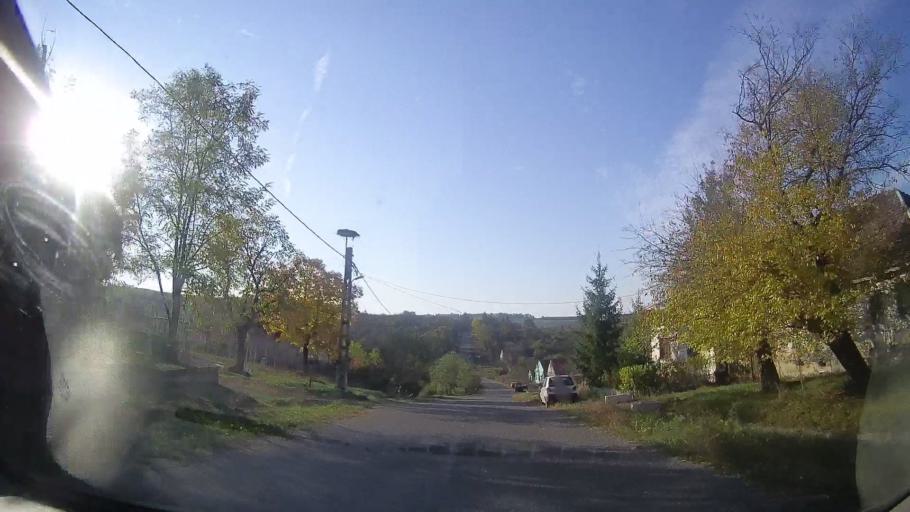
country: RO
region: Timis
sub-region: Comuna Bogda
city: Bogda
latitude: 45.9605
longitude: 21.6143
